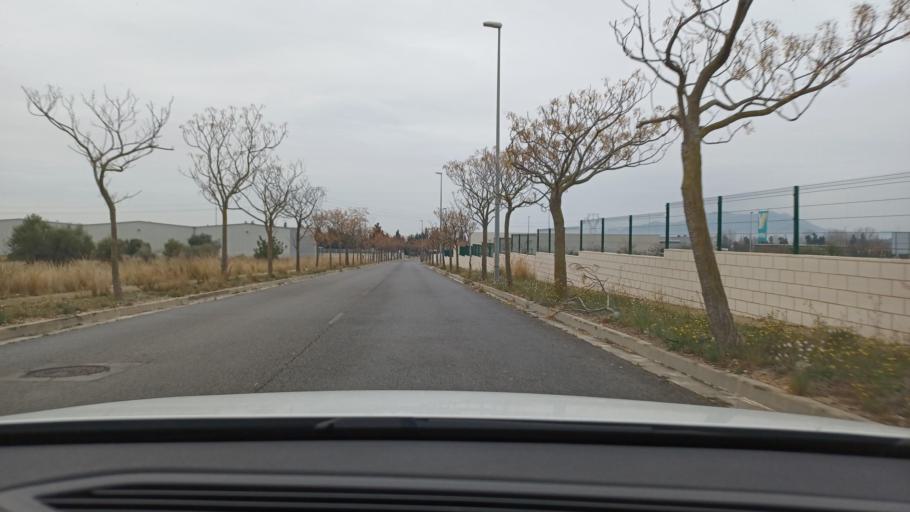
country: ES
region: Catalonia
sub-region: Provincia de Tarragona
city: Amposta
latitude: 40.7591
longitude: 0.6003
